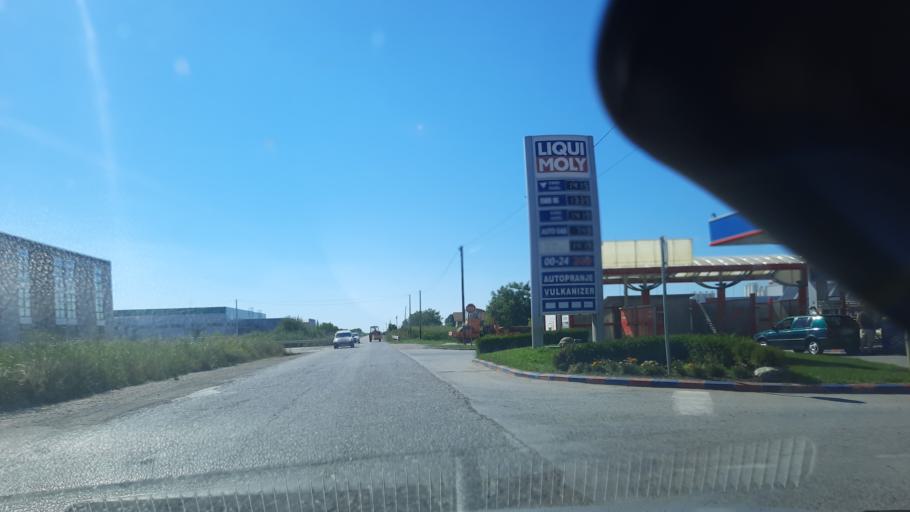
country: RS
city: Simanovci
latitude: 44.8771
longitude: 20.0718
